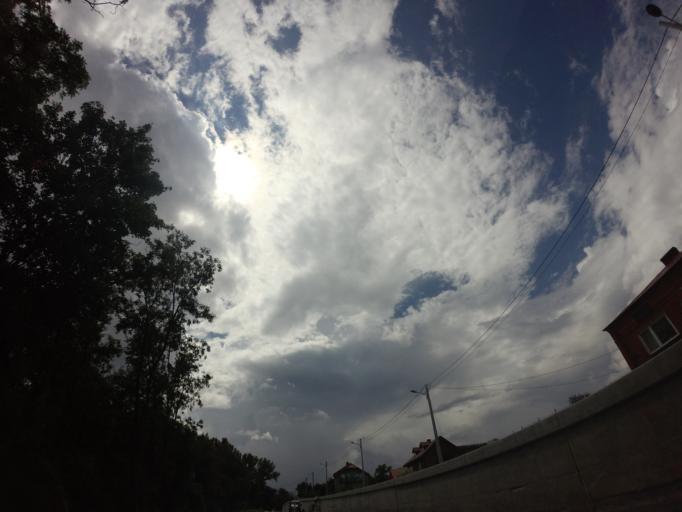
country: PL
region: Swietokrzyskie
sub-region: Powiat opatowski
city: Tarlow
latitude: 51.0407
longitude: 21.6968
